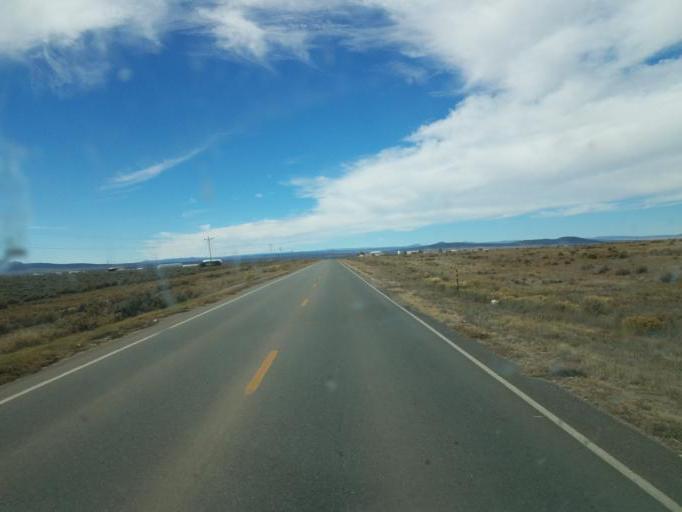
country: US
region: New Mexico
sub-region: Taos County
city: Taos
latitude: 36.4630
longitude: -105.6533
